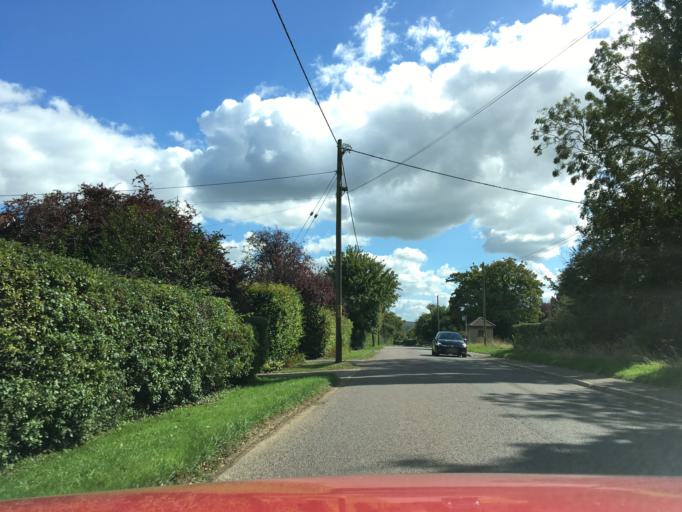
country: GB
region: England
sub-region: Wiltshire
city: Bratton
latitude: 51.3171
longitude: -2.1427
